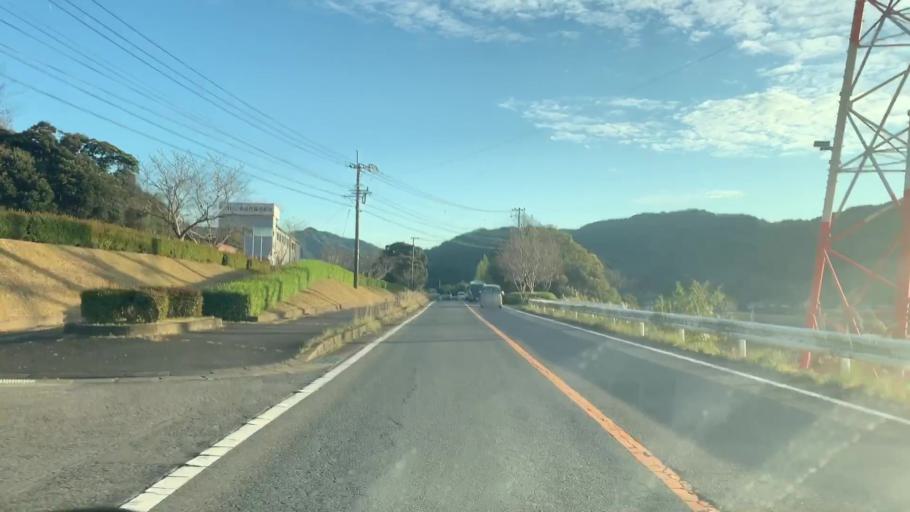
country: JP
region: Saga Prefecture
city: Karatsu
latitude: 33.3857
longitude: 129.9883
